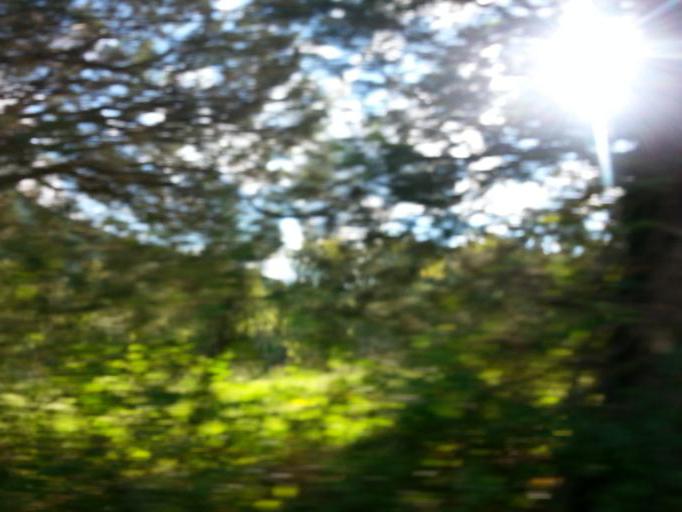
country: US
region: Tennessee
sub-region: Grainger County
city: Blaine
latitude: 36.1340
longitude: -83.7530
